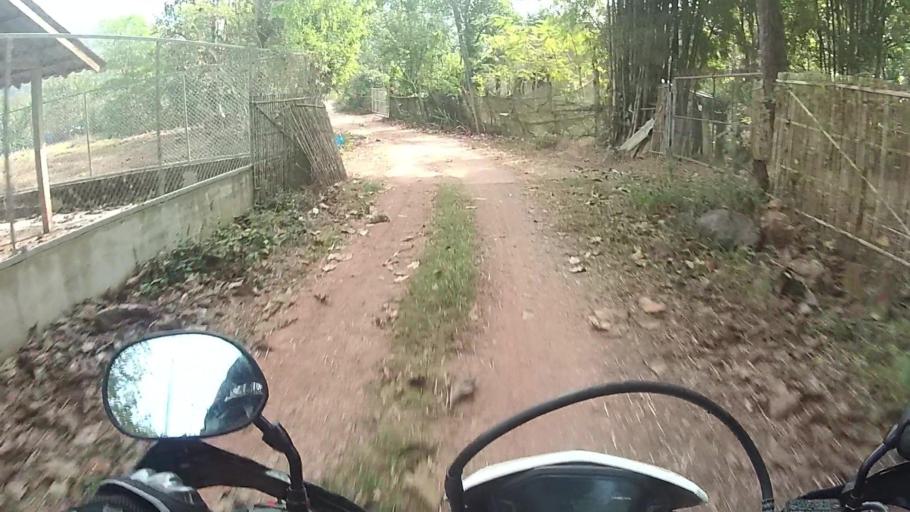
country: TH
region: Chiang Mai
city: Mae On
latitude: 18.7228
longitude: 99.2986
